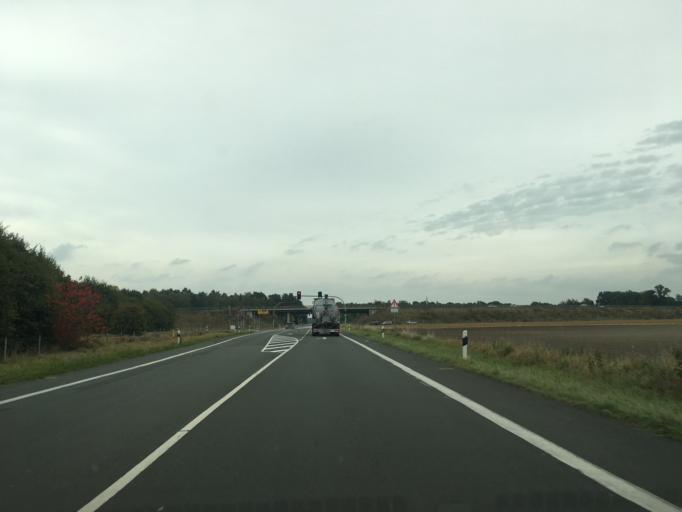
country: DE
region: North Rhine-Westphalia
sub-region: Regierungsbezirk Munster
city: Metelen
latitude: 52.1689
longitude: 7.2597
